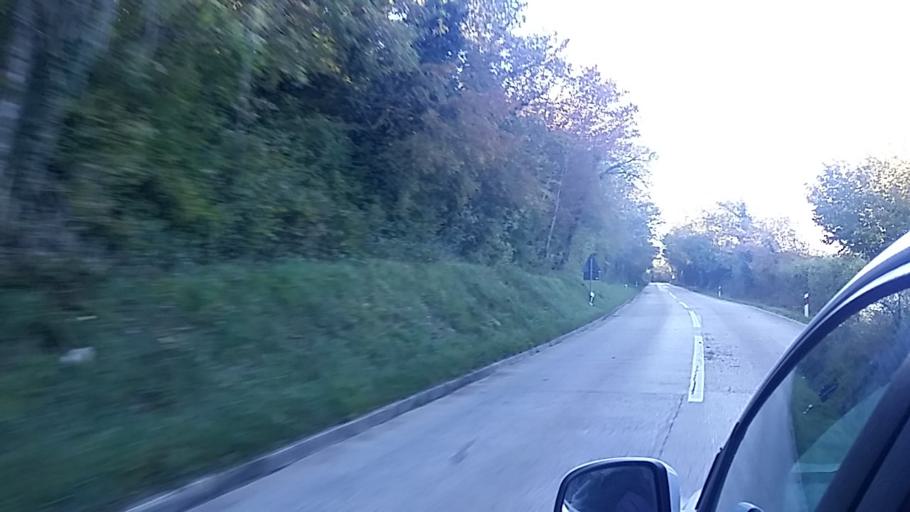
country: HR
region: Istarska
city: Vrsar
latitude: 45.1533
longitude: 13.6472
